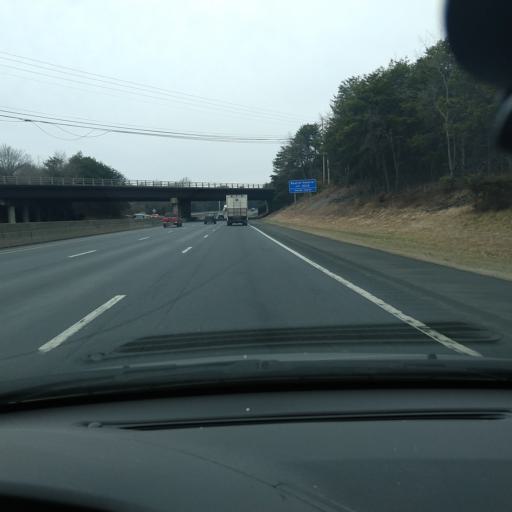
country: US
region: North Carolina
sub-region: Forsyth County
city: Winston-Salem
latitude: 36.0585
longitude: -80.2123
